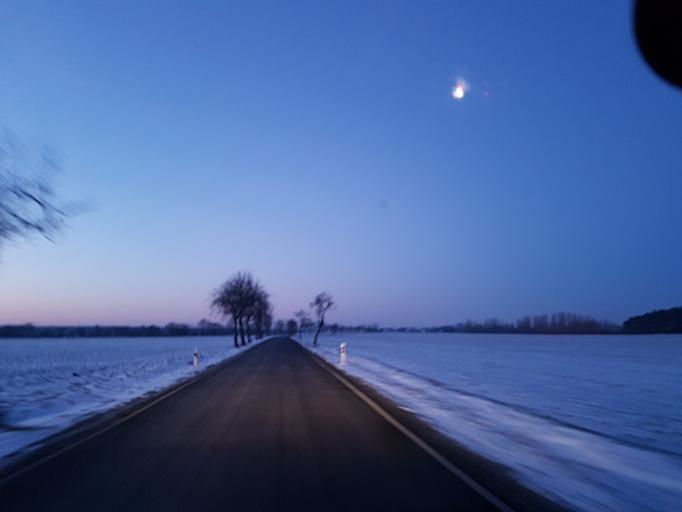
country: DE
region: Brandenburg
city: Falkenberg
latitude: 51.5129
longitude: 13.2961
